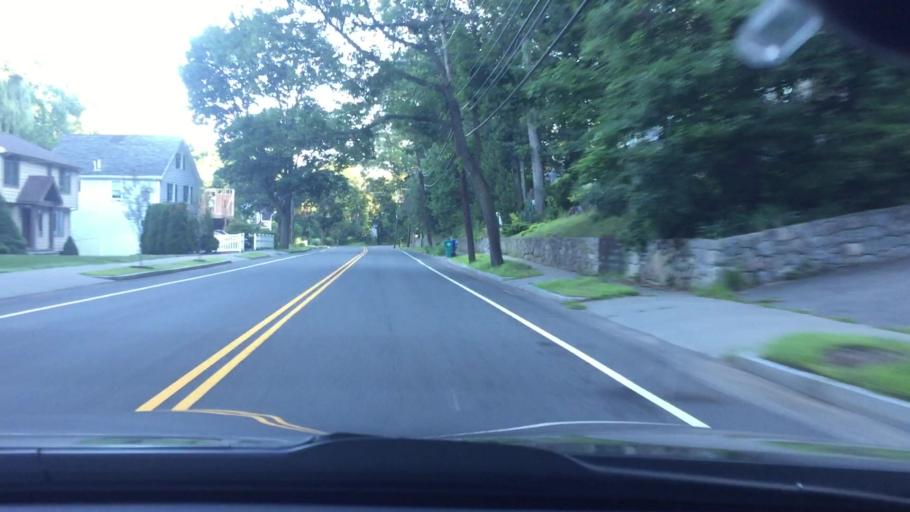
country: US
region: Massachusetts
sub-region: Middlesex County
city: Newton
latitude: 42.3109
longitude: -71.2084
